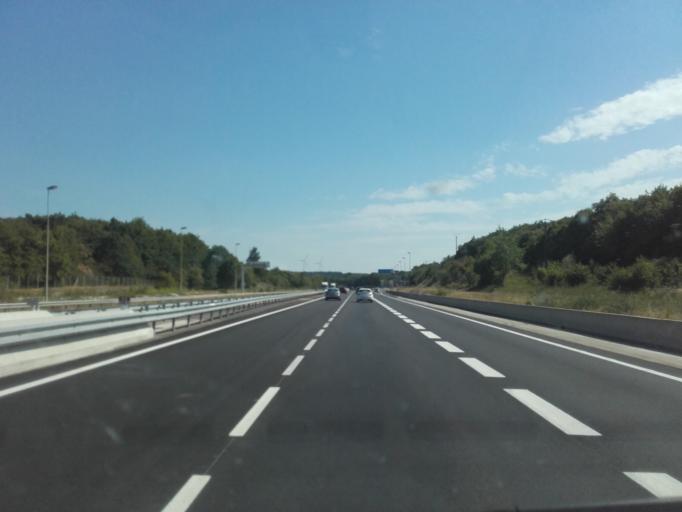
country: FR
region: Bourgogne
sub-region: Departement de la Cote-d'Or
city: Savigny-les-Beaune
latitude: 47.1107
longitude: 4.7121
